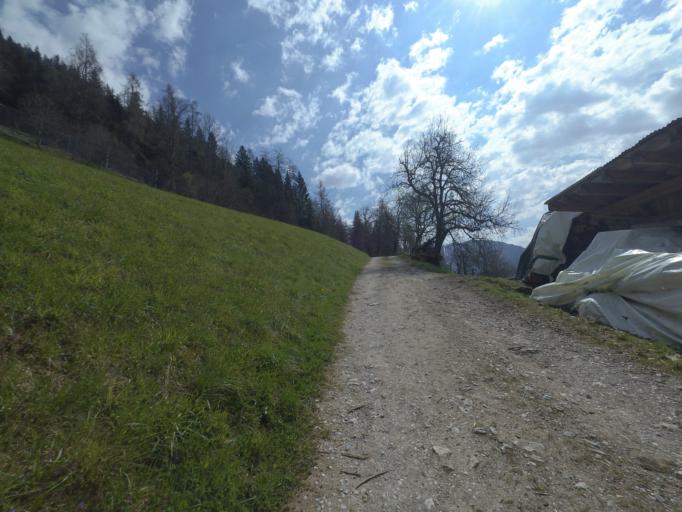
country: AT
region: Salzburg
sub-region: Politischer Bezirk Sankt Johann im Pongau
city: Sankt Veit im Pongau
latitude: 47.3355
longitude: 13.1576
